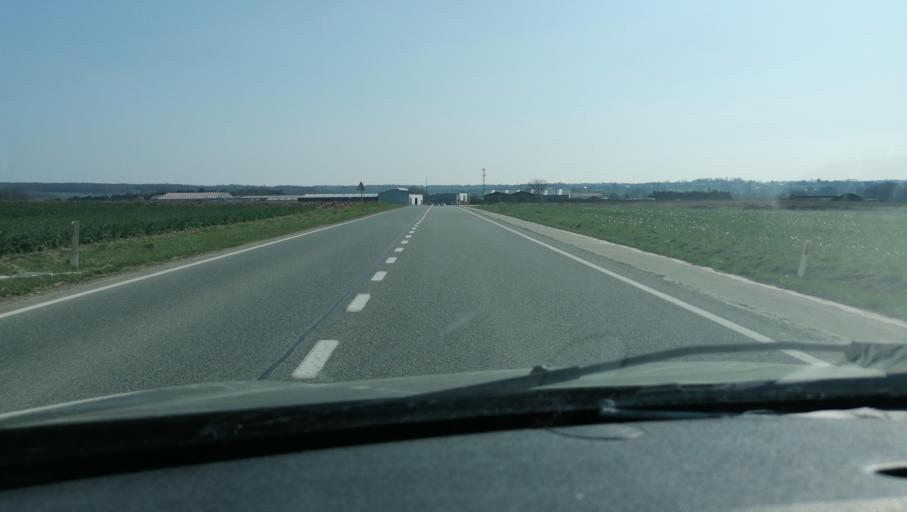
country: BE
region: Wallonia
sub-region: Province du Hainaut
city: Chimay
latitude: 50.0424
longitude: 4.3784
